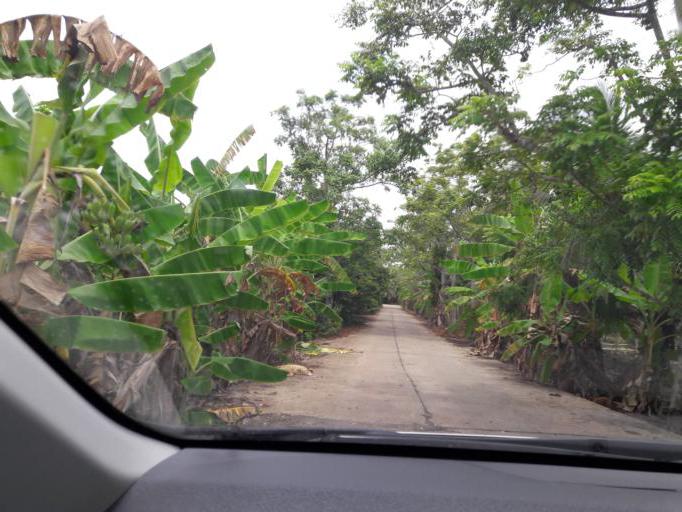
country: TH
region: Ratchaburi
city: Damnoen Saduak
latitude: 13.5475
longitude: 100.0063
